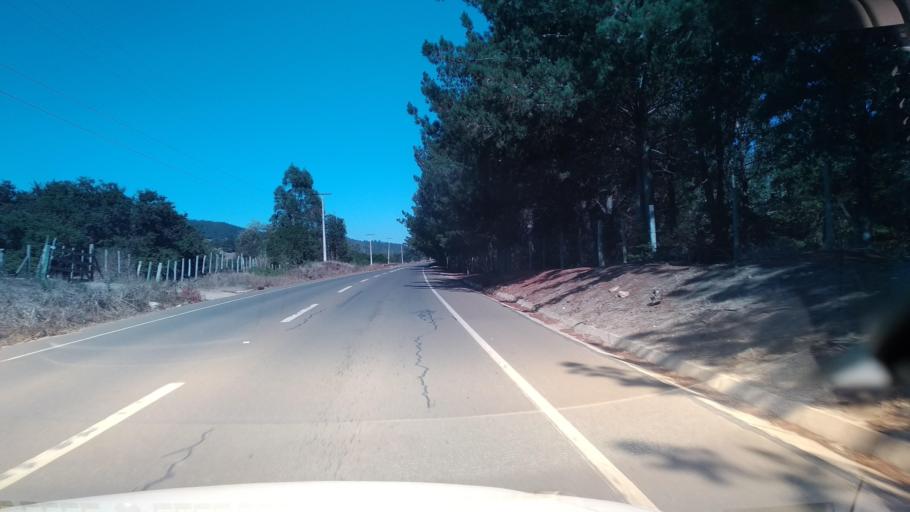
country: CL
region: O'Higgins
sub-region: Provincia de Colchagua
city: Santa Cruz
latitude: -34.4562
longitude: -72.0265
